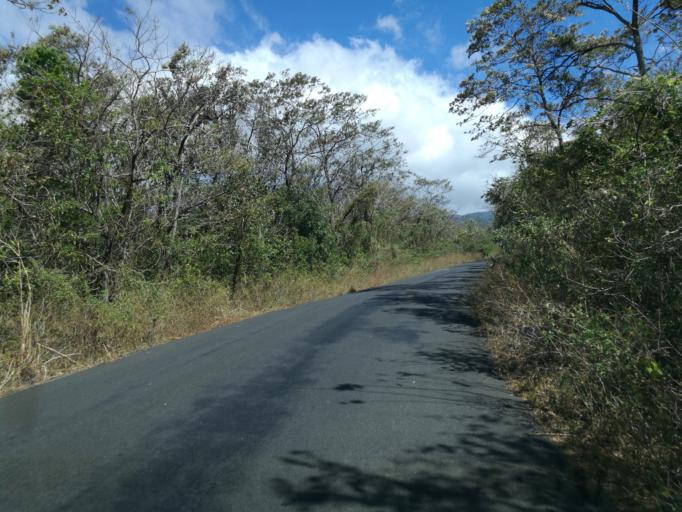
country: CR
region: Guanacaste
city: Liberia
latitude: 10.7536
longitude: -85.3730
